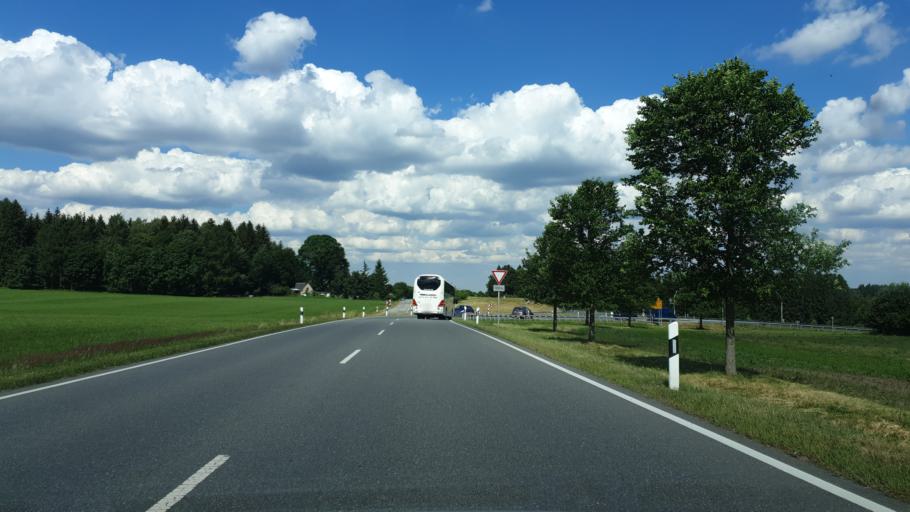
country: DE
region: Saxony
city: Marienberg
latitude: 50.6673
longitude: 13.1373
